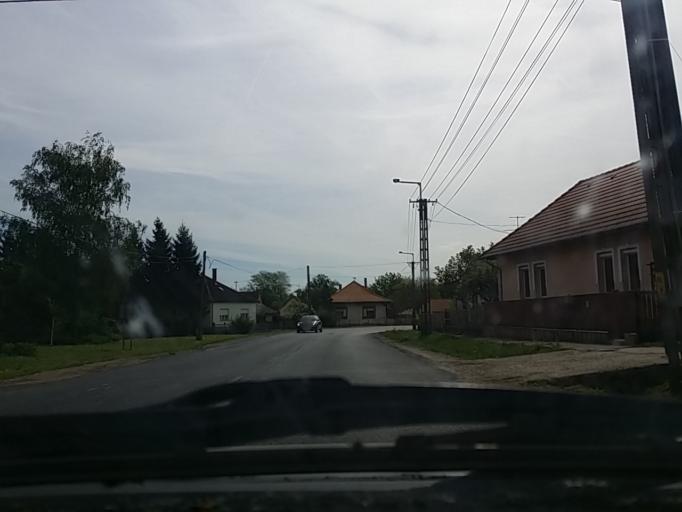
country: HU
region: Somogy
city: Csurgo
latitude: 46.2398
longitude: 17.1116
